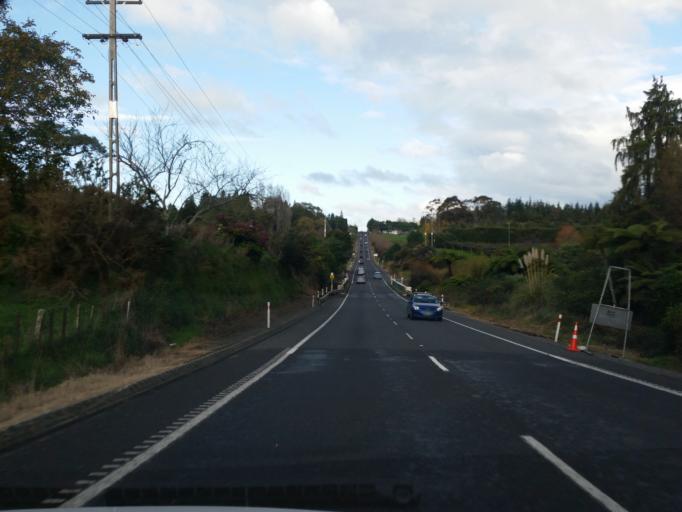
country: NZ
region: Bay of Plenty
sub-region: Western Bay of Plenty District
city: Katikati
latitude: -37.6576
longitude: 176.0021
